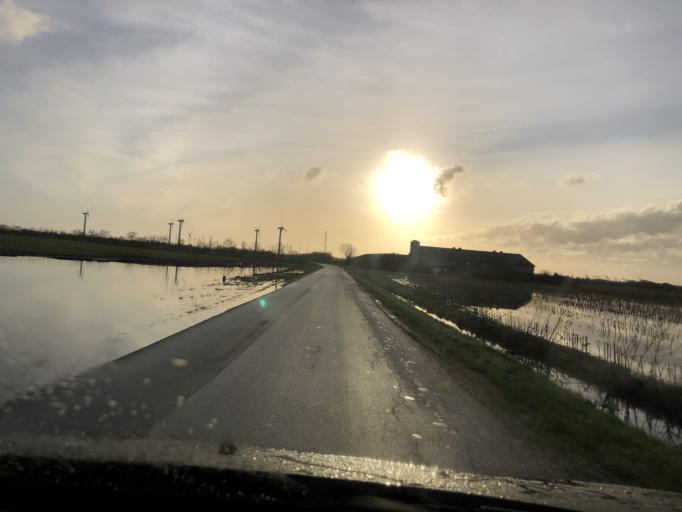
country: DK
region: Central Jutland
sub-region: Ringkobing-Skjern Kommune
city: Skjern
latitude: 55.8705
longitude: 8.3546
